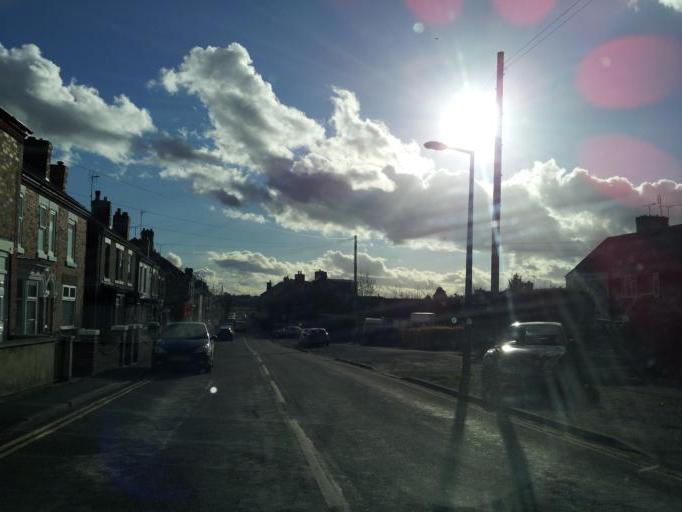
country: GB
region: England
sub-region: Derbyshire
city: Alfreton
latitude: 53.1158
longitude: -1.3708
